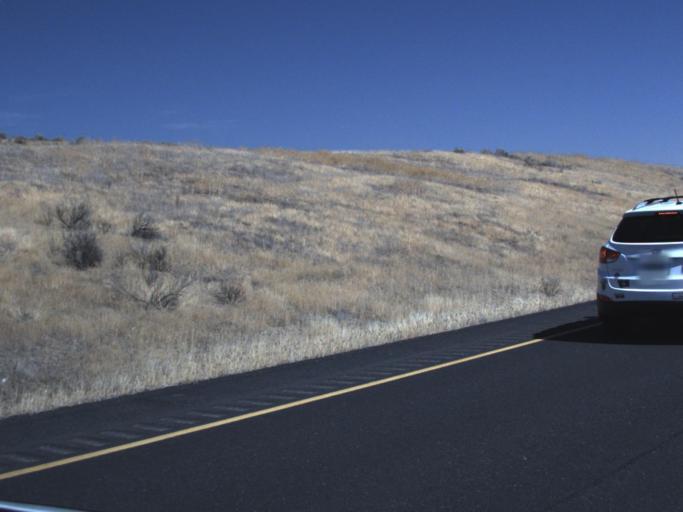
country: US
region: Washington
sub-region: Grant County
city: Warden
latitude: 47.0872
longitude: -118.9114
